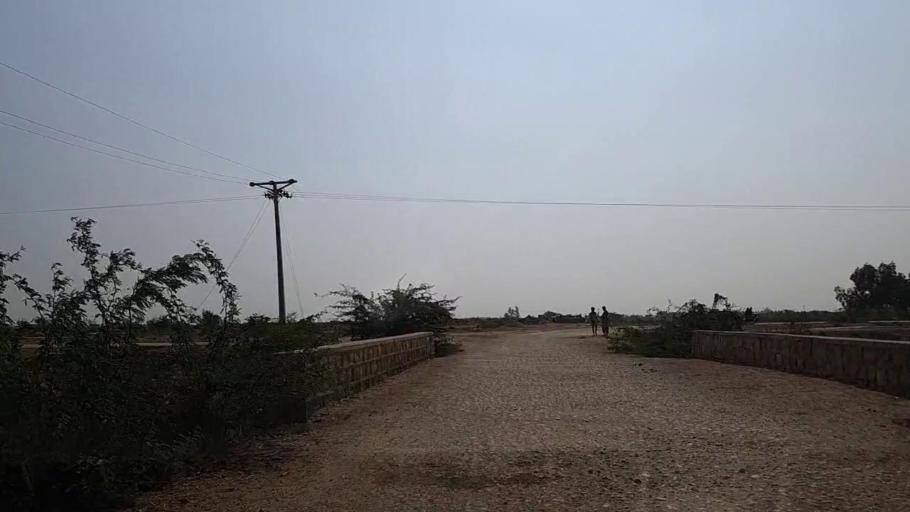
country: PK
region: Sindh
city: Thatta
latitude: 24.7115
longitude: 67.7685
